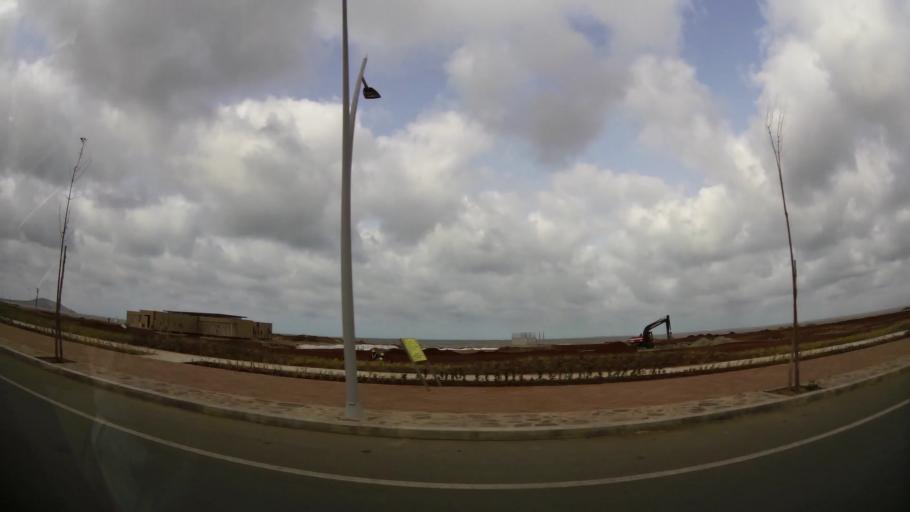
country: MA
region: Oriental
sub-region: Nador
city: Nador
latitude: 35.1608
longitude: -2.9069
